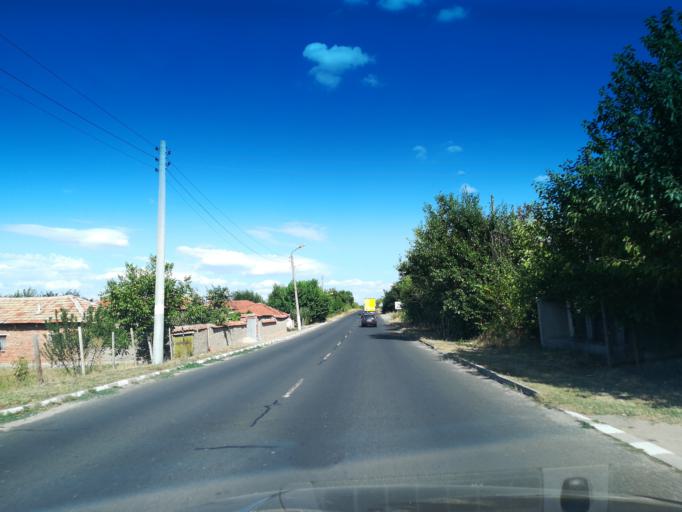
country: BG
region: Stara Zagora
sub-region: Obshtina Chirpan
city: Chirpan
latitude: 42.0589
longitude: 25.2725
